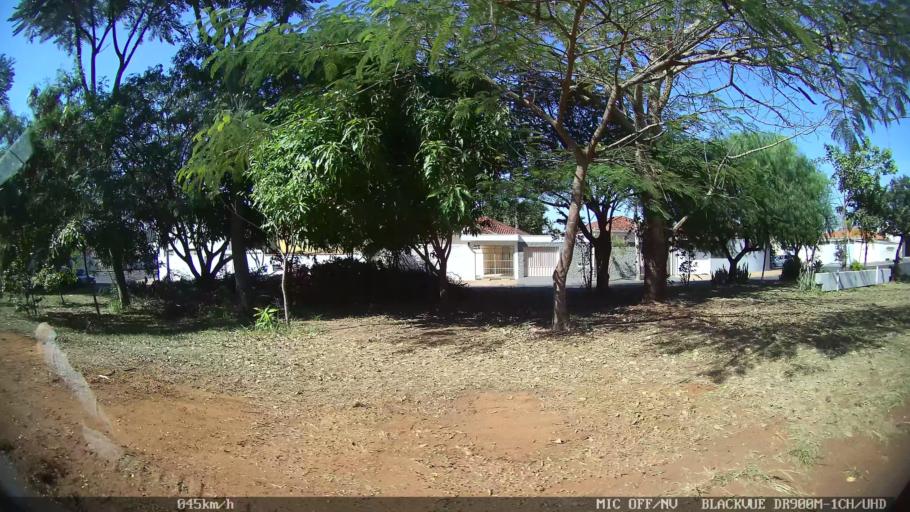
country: BR
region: Sao Paulo
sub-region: Batatais
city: Batatais
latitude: -20.8781
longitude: -47.5972
